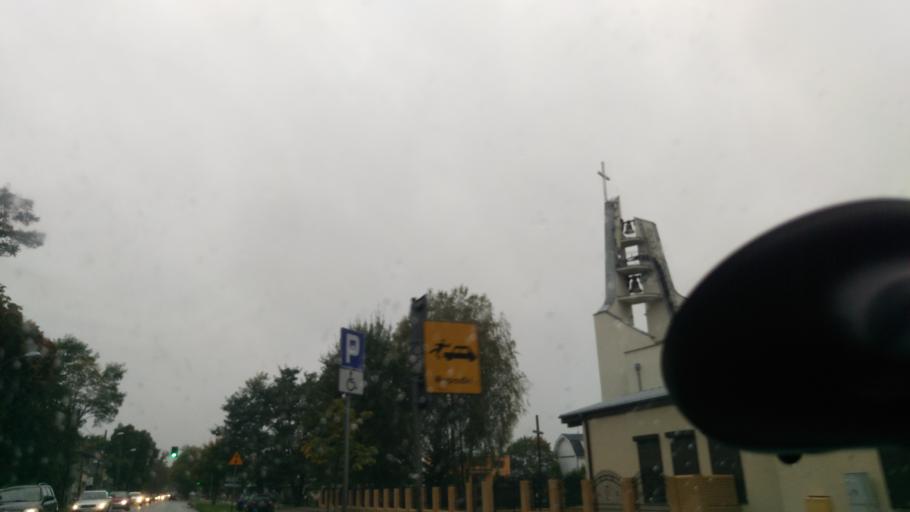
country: PL
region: West Pomeranian Voivodeship
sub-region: Szczecin
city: Szczecin
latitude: 53.4000
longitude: 14.6836
